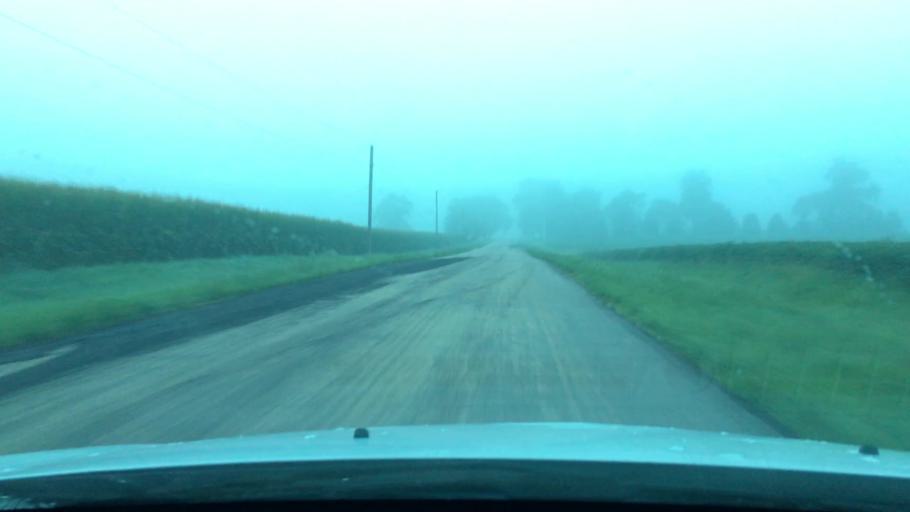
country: US
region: Illinois
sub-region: Ogle County
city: Rochelle
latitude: 41.9125
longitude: -88.9805
